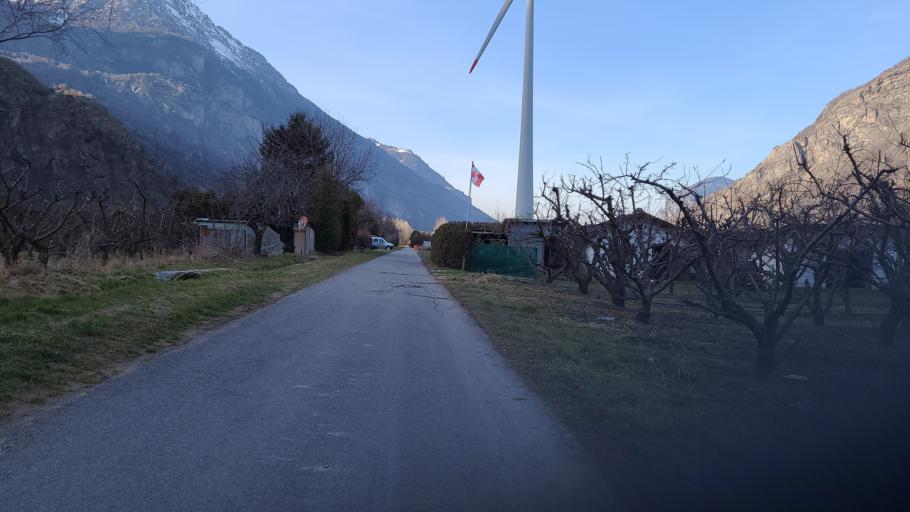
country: CH
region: Valais
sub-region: Saint-Maurice District
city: Vernayaz
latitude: 46.1248
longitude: 7.0536
